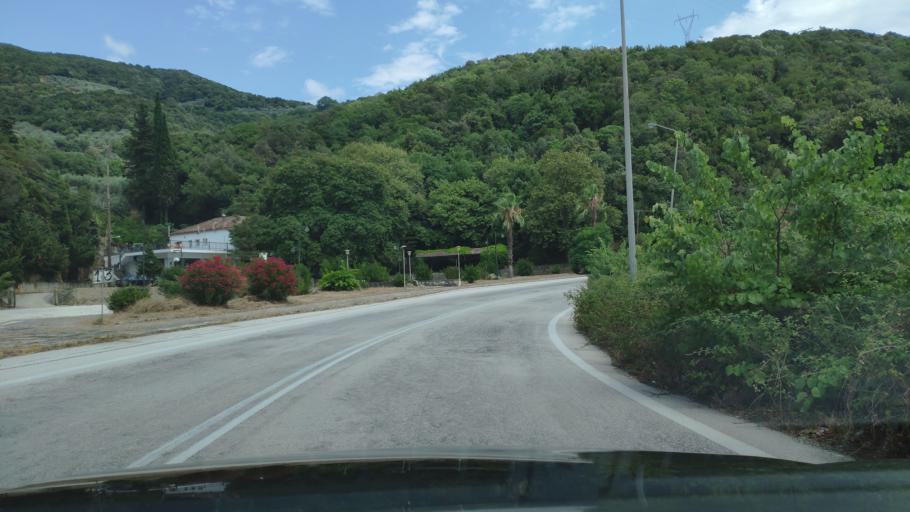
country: GR
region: West Greece
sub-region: Nomos Aitolias kai Akarnanias
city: Menidi
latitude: 39.0233
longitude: 21.1342
